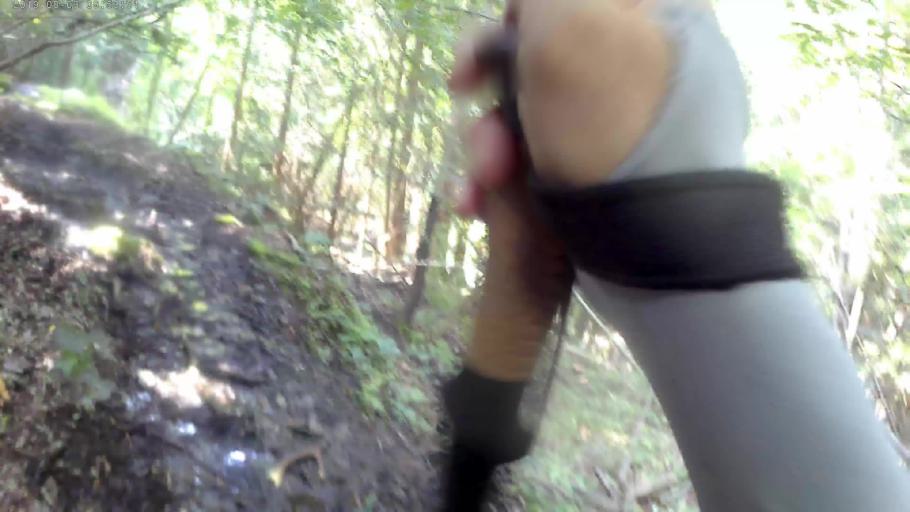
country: JP
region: Yamanashi
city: Enzan
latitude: 35.6332
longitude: 138.7689
